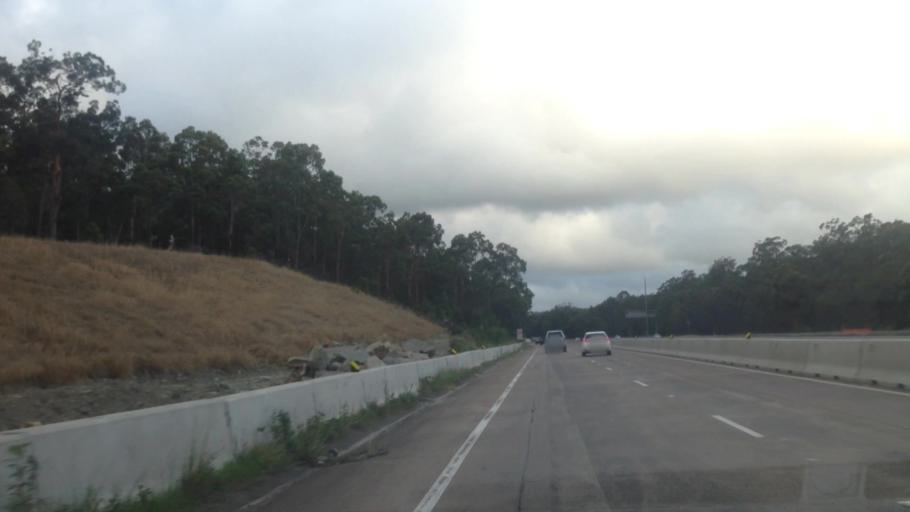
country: AU
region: New South Wales
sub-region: Wyong Shire
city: Jilliby
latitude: -33.2190
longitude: 151.4409
